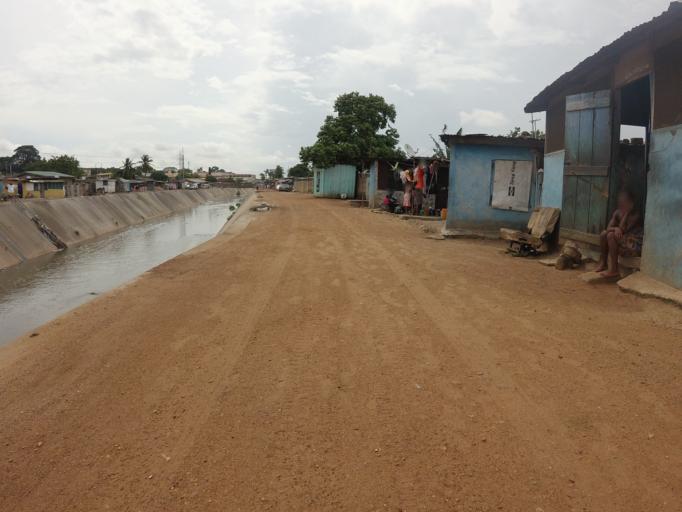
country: GH
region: Greater Accra
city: Accra
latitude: 5.5932
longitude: -0.2180
